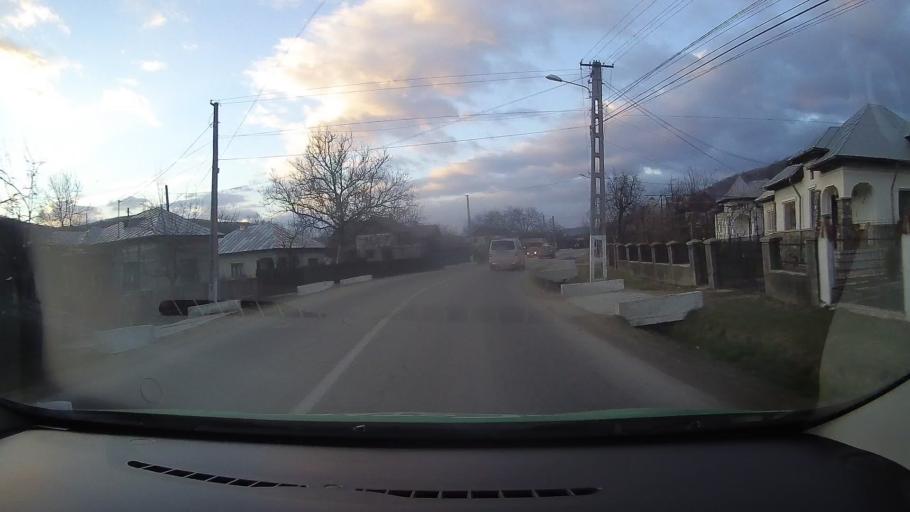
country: RO
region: Dambovita
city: Iedera de Jos
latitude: 45.0156
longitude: 25.6407
